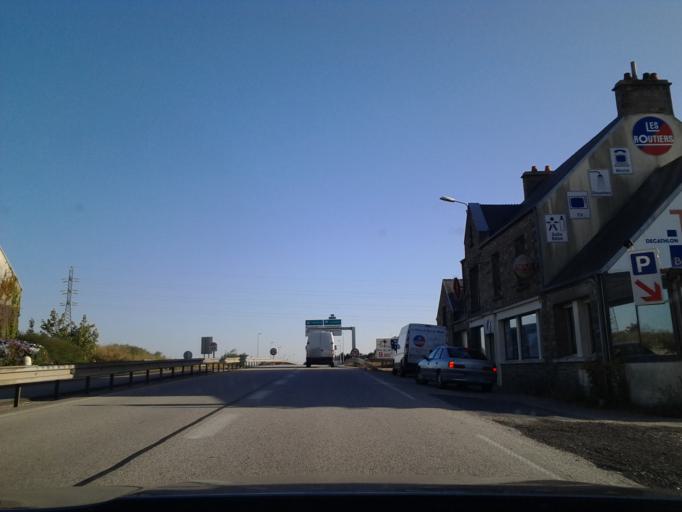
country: FR
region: Lower Normandy
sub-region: Departement de la Manche
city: La Glacerie
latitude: 49.5955
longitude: -1.5960
